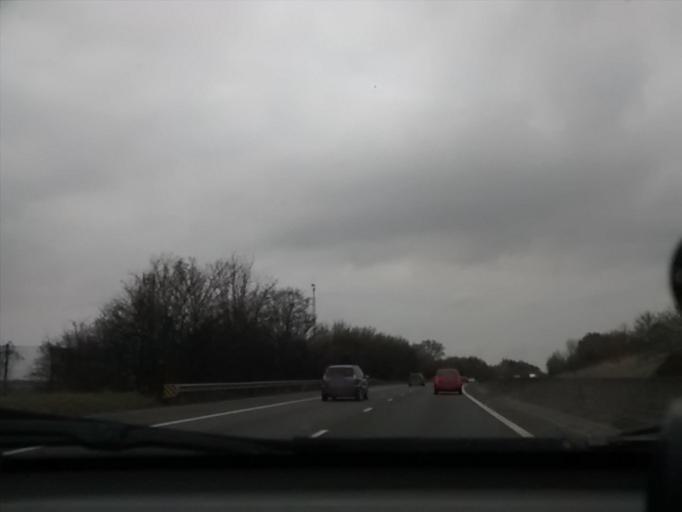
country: GB
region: England
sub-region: Essex
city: Elsenham
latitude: 51.9680
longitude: 0.2144
